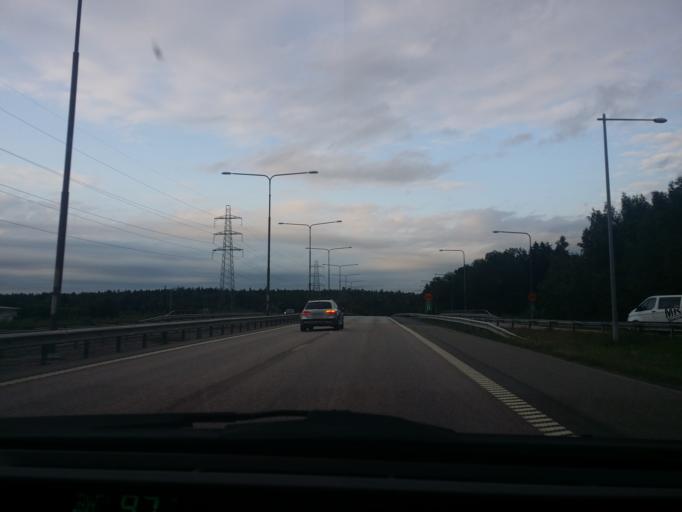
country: SE
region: Vaestmanland
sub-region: Vasteras
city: Vasteras
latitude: 59.6108
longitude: 16.4736
